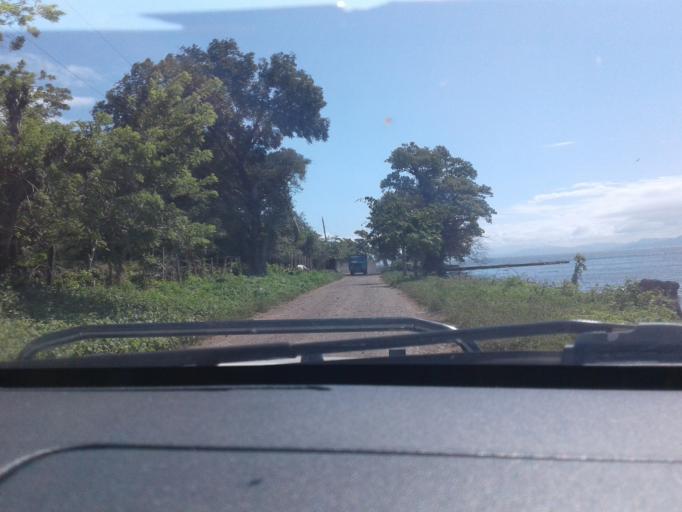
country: NI
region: Rivas
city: Altagracia
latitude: 11.4170
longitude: -85.5415
